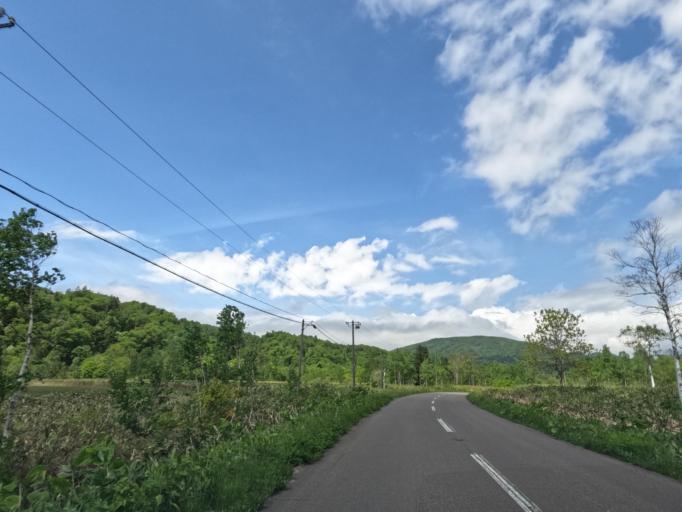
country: JP
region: Hokkaido
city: Tobetsu
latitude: 43.5236
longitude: 141.5874
